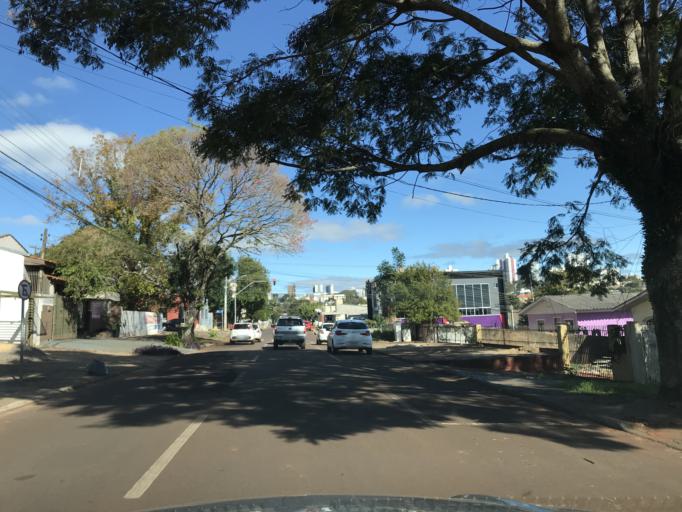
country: BR
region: Parana
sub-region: Cascavel
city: Cascavel
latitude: -24.9429
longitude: -53.4685
